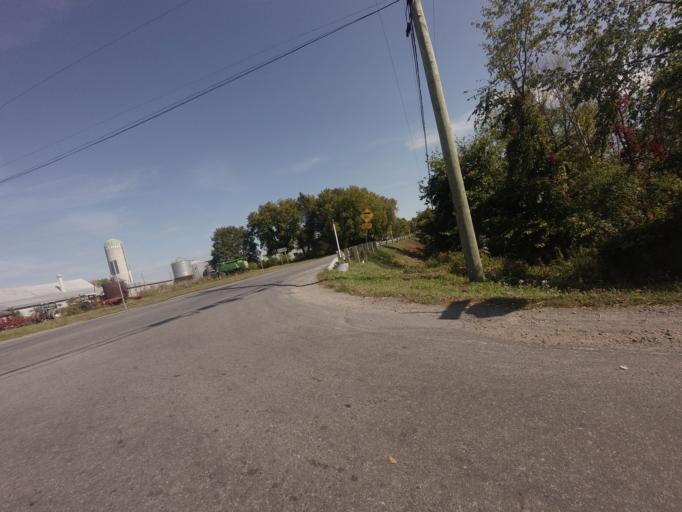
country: CA
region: Quebec
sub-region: Laurentides
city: Saint-Eustache
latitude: 45.5931
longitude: -73.9073
